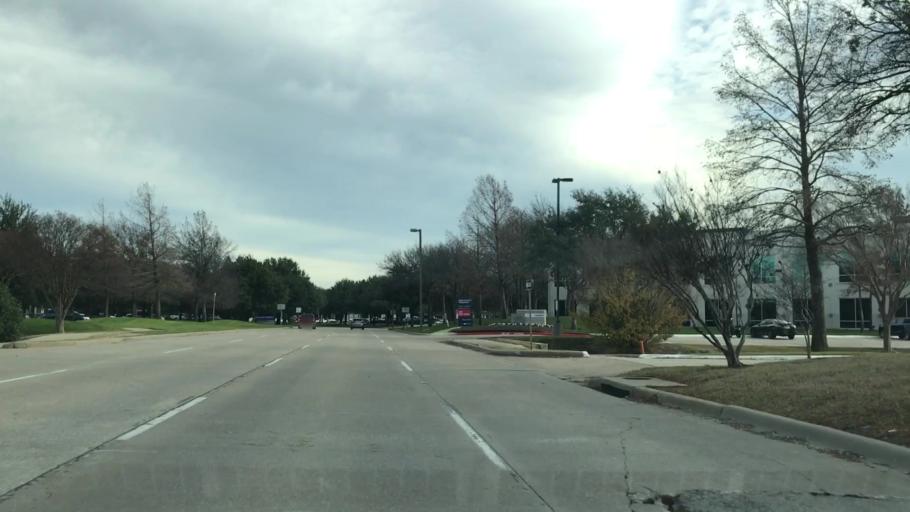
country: US
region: Texas
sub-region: Dallas County
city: Coppell
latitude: 32.9249
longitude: -97.0139
